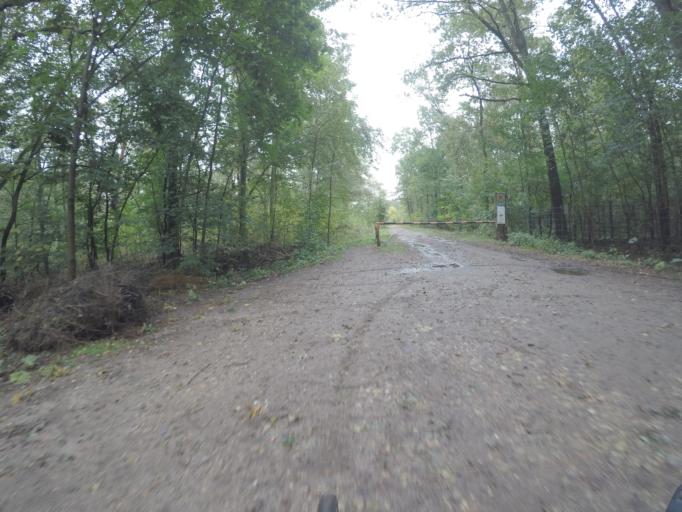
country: DE
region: Berlin
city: Buch
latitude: 52.6532
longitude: 13.4910
